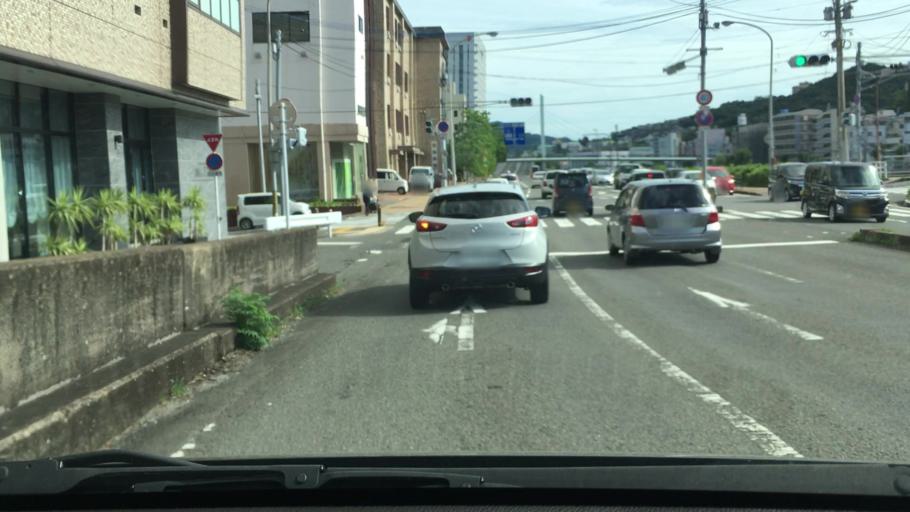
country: JP
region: Nagasaki
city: Nagasaki-shi
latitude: 32.7691
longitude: 129.8625
